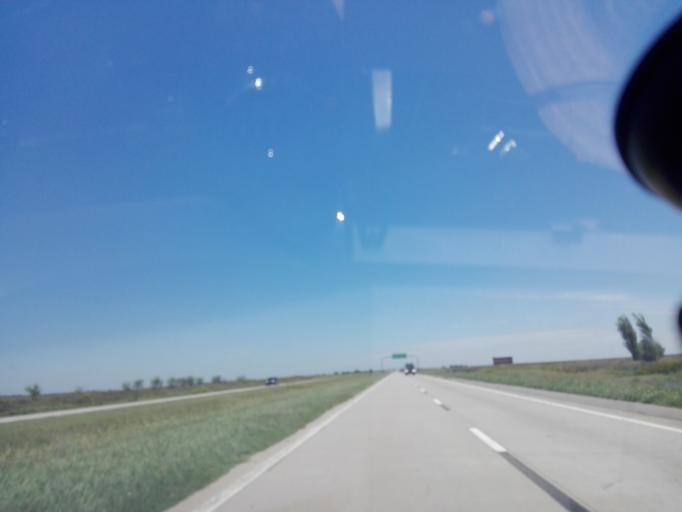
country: AR
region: Cordoba
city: Morrison
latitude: -32.5662
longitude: -62.8043
